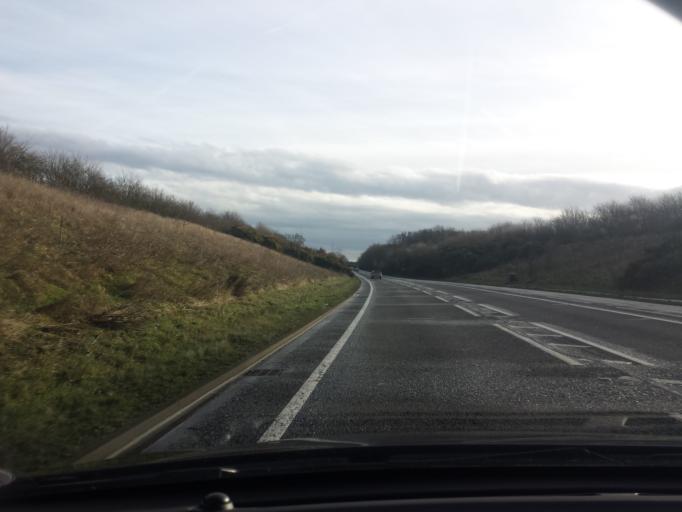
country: GB
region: England
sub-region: Essex
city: Great Bentley
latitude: 51.8472
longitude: 1.1048
